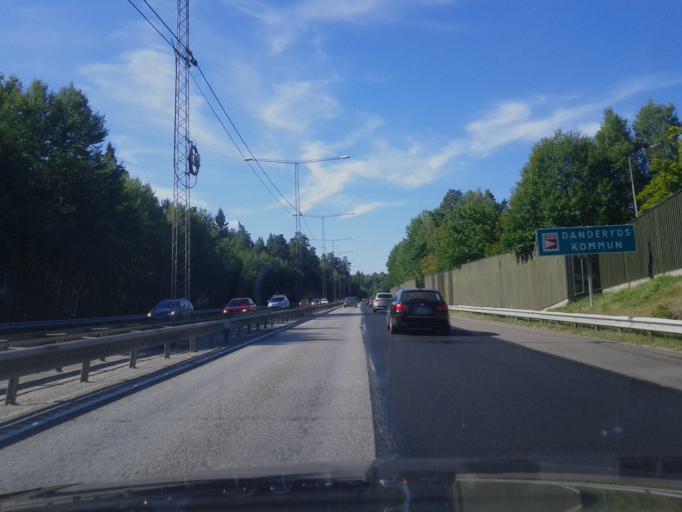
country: SE
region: Stockholm
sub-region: Taby Kommun
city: Taby
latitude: 59.4239
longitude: 18.0563
